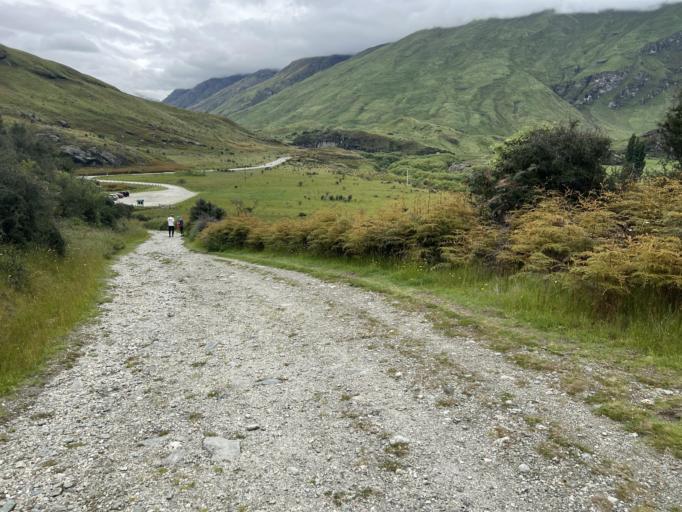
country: NZ
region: Otago
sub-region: Queenstown-Lakes District
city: Wanaka
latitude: -44.6495
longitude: 168.9597
